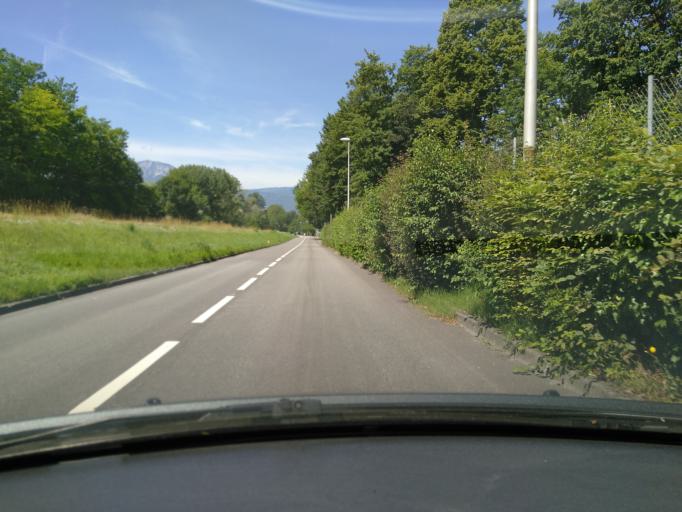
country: FR
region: Rhone-Alpes
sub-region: Departement de l'Isere
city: Corenc
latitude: 45.2044
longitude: 5.7777
